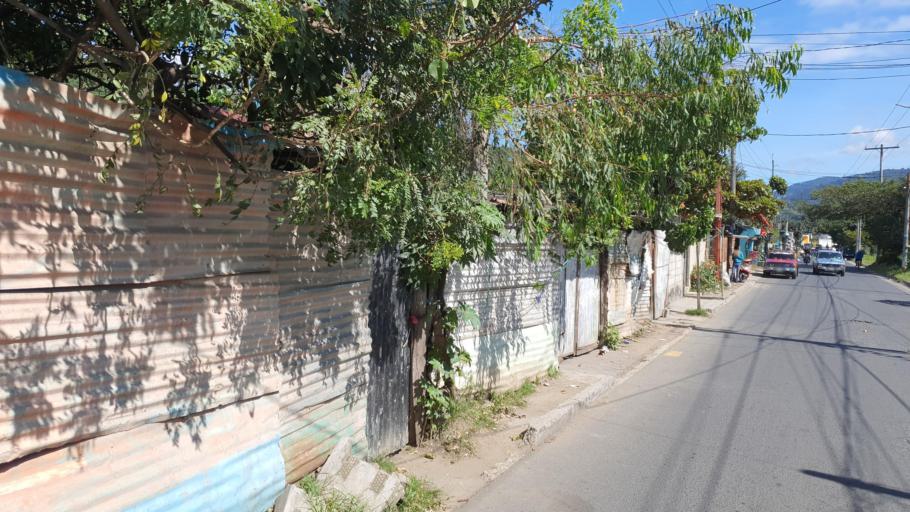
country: GT
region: Guatemala
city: Villa Canales
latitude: 14.4741
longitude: -90.5401
